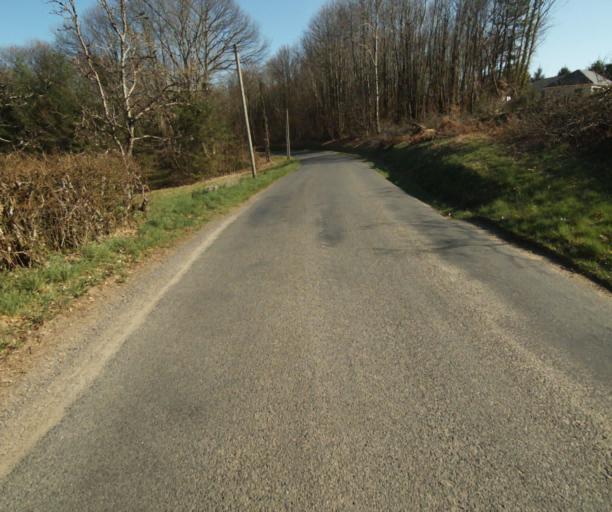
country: FR
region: Limousin
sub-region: Departement de la Correze
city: Saint-Mexant
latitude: 45.2954
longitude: 1.6953
